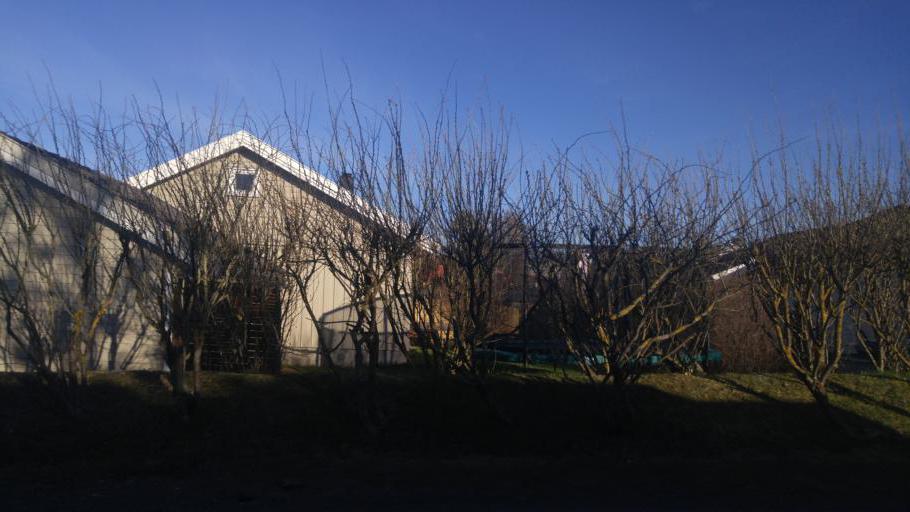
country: NO
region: Sor-Trondelag
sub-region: Trondheim
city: Trondheim
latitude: 63.4256
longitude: 10.4586
